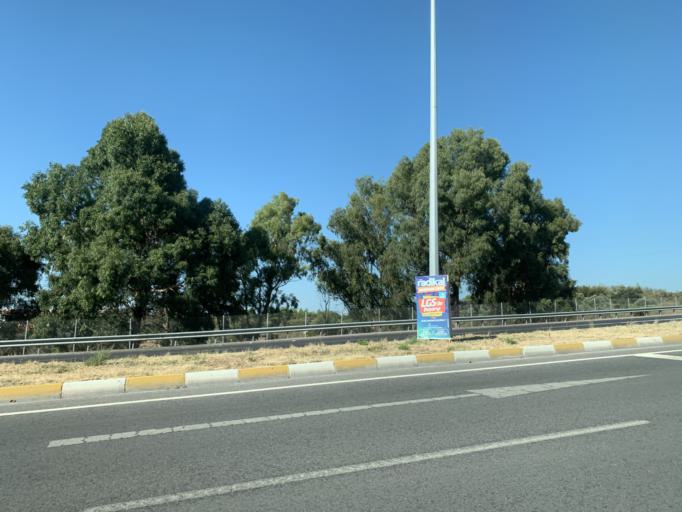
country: TR
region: Izmir
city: Urla
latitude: 38.3256
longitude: 26.7808
